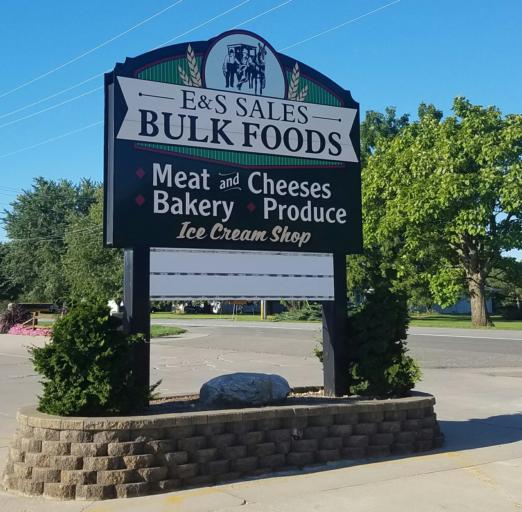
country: US
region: Indiana
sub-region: LaGrange County
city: Topeka
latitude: 41.6587
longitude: -85.5800
